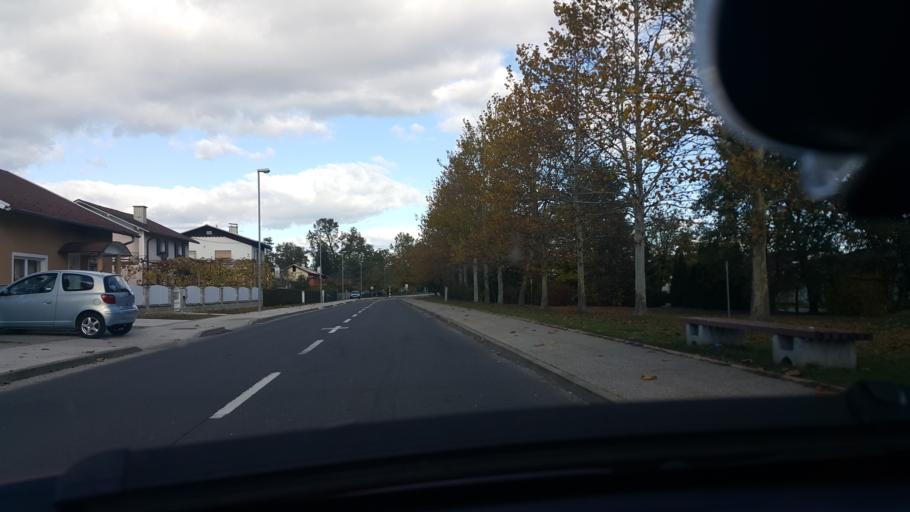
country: SI
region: Hoce-Slivnica
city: Rogoza
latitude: 46.5264
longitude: 15.6794
